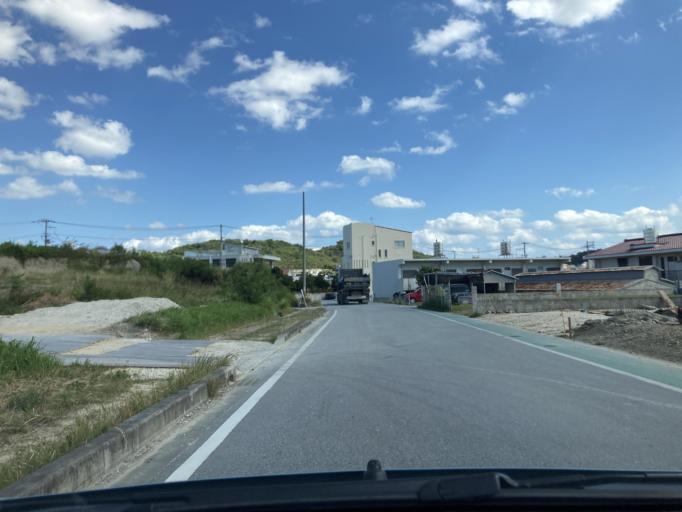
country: JP
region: Okinawa
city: Tomigusuku
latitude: 26.1882
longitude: 127.7117
